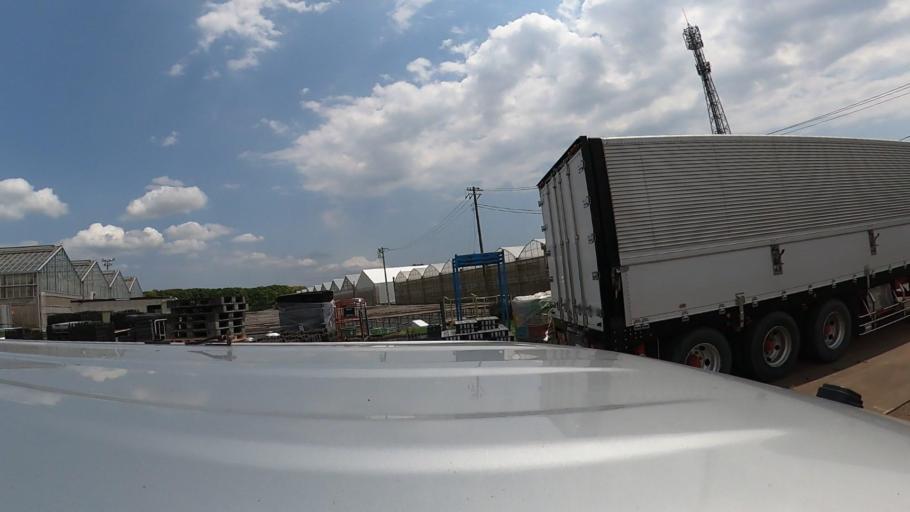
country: JP
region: Kanagawa
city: Chigasaki
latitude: 35.3896
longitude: 139.4216
